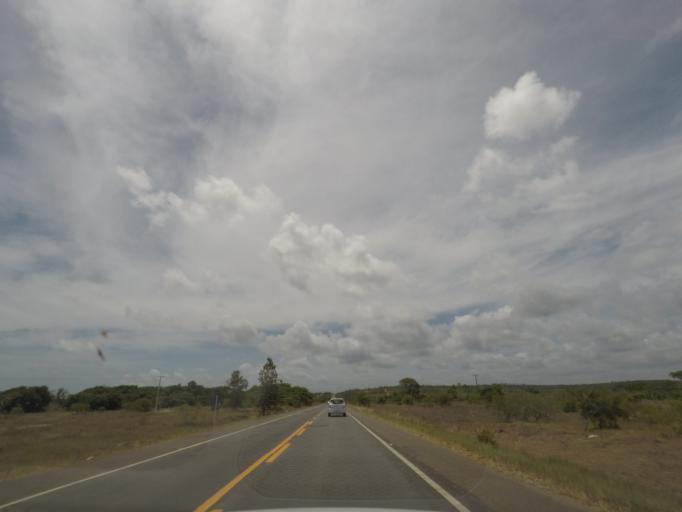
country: BR
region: Bahia
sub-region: Conde
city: Conde
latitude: -11.8719
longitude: -37.6359
